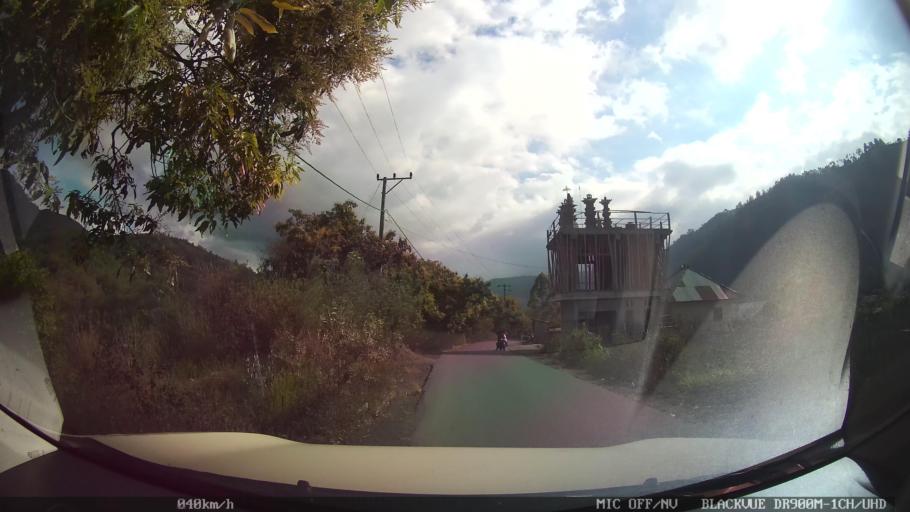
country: ID
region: Bali
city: Banjar Kedisan
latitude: -8.2173
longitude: 115.3687
